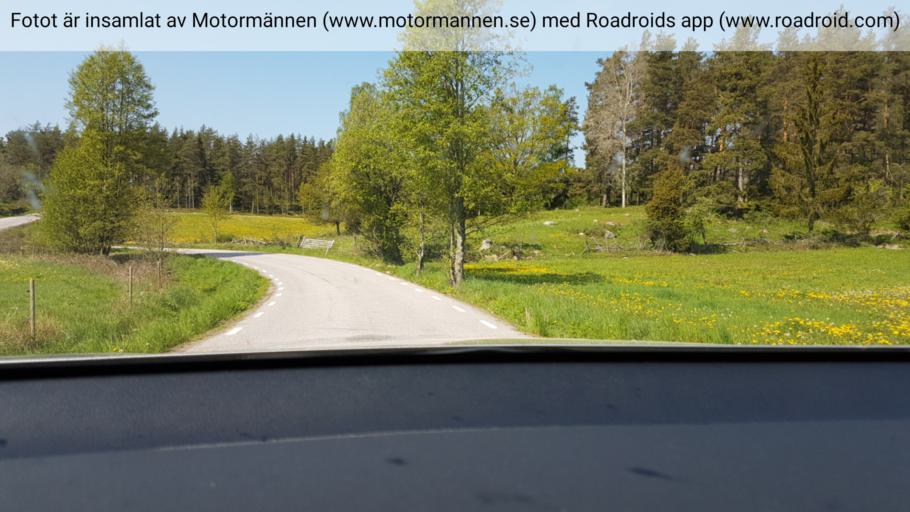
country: SE
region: Kalmar
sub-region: Vasterviks Kommun
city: Forserum
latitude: 57.8693
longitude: 16.4834
